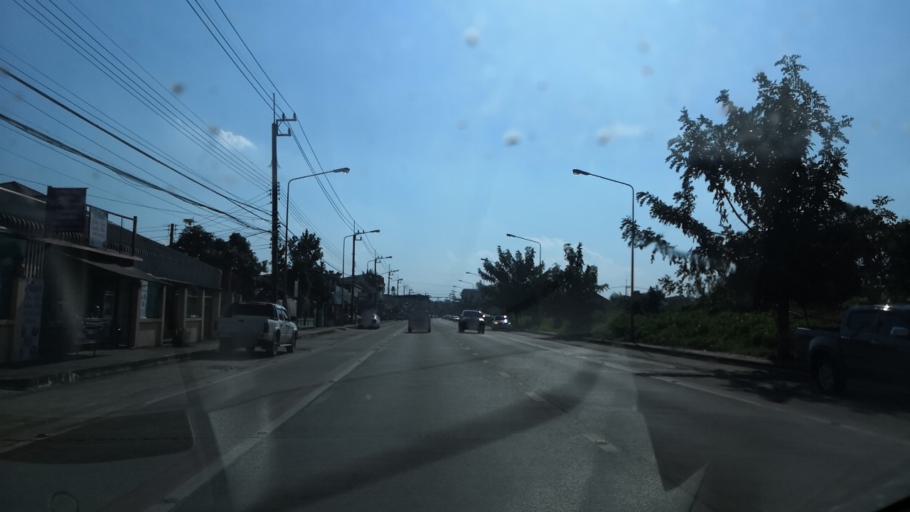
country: TH
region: Chiang Rai
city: Chiang Rai
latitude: 19.9310
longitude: 99.8398
